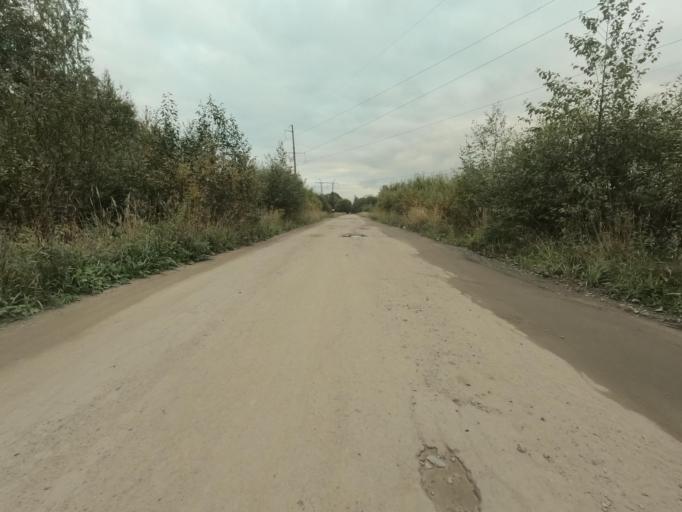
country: RU
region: St.-Petersburg
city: Sapernyy
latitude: 59.7597
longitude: 30.6560
